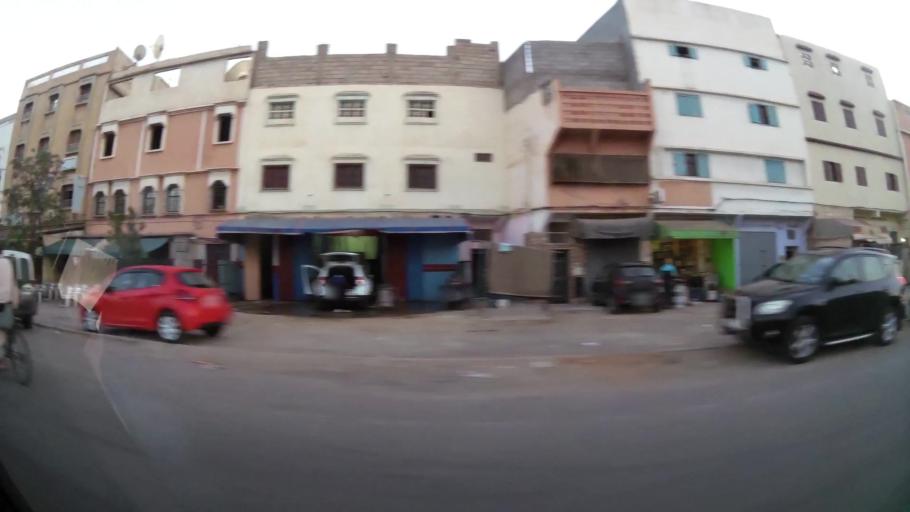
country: MA
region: Souss-Massa-Draa
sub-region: Inezgane-Ait Mellou
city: Inezgane
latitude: 30.3768
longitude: -9.4970
